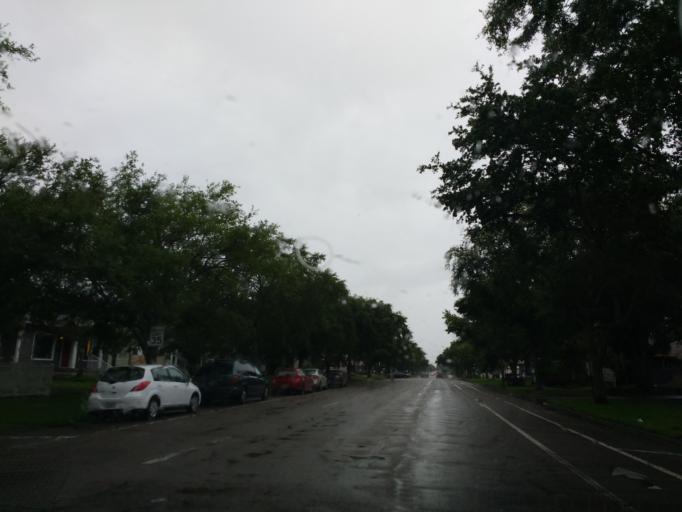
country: US
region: Florida
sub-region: Pinellas County
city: Saint Petersburg
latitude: 27.7719
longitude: -82.6715
